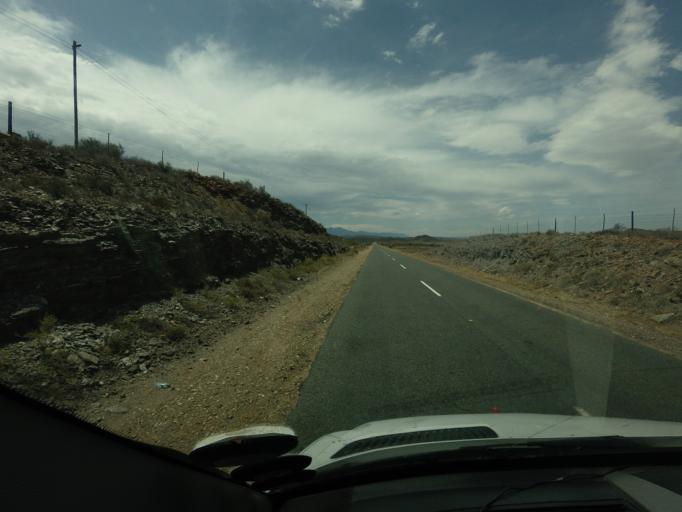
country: ZA
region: Western Cape
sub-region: Eden District Municipality
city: Ladismith
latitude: -33.6660
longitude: 20.9968
